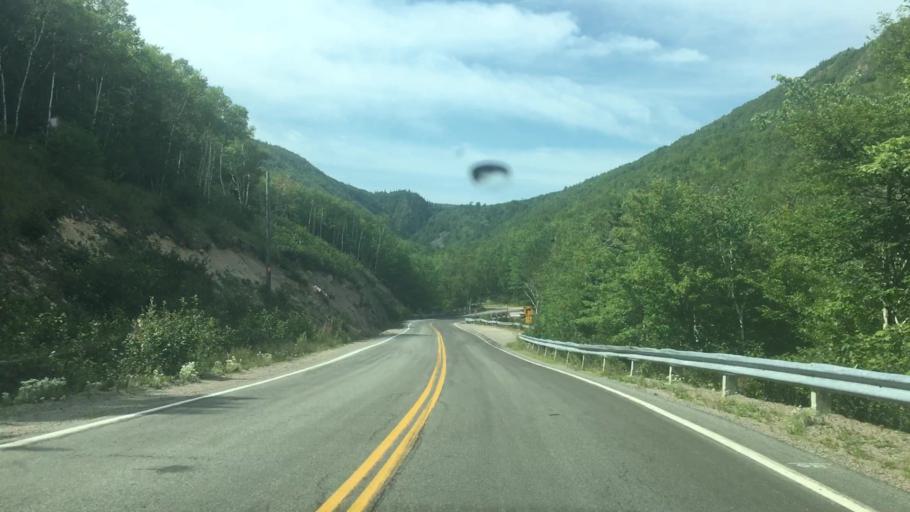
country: CA
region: Nova Scotia
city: Sydney Mines
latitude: 46.5827
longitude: -60.3946
